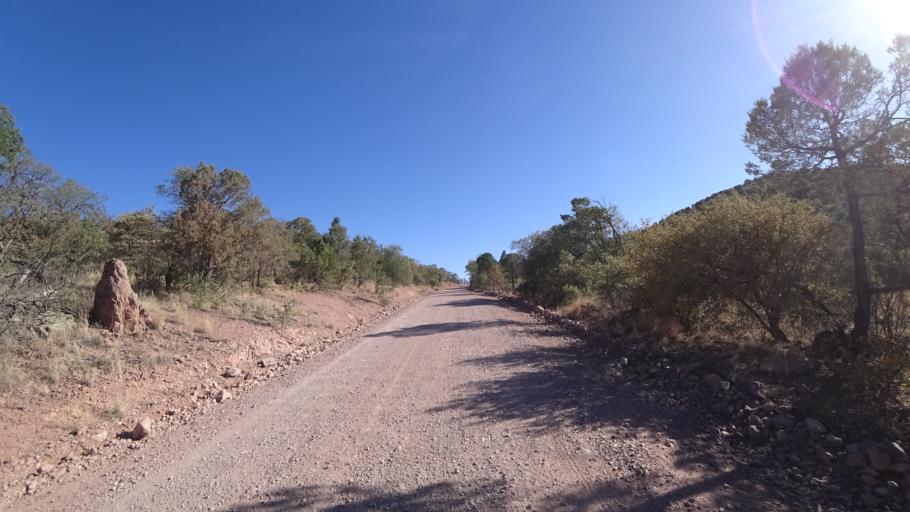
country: US
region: Arizona
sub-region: Cochise County
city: Huachuca City
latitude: 31.5017
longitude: -110.5585
